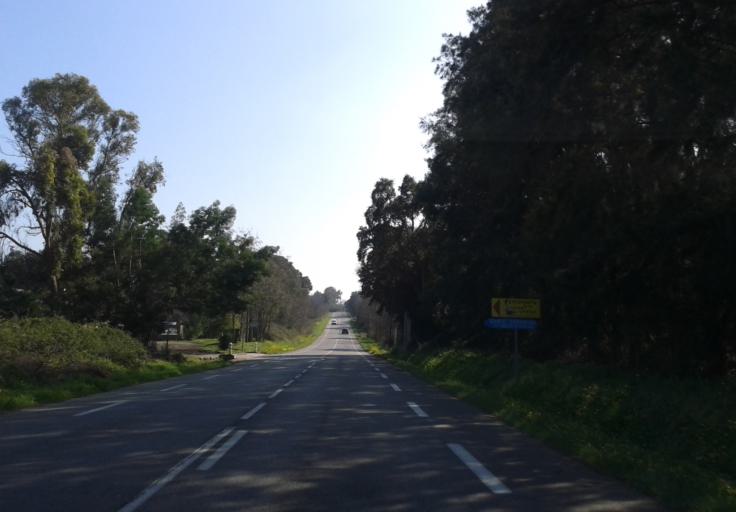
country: FR
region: Corsica
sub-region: Departement de la Haute-Corse
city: Cervione
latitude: 42.3016
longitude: 9.5445
